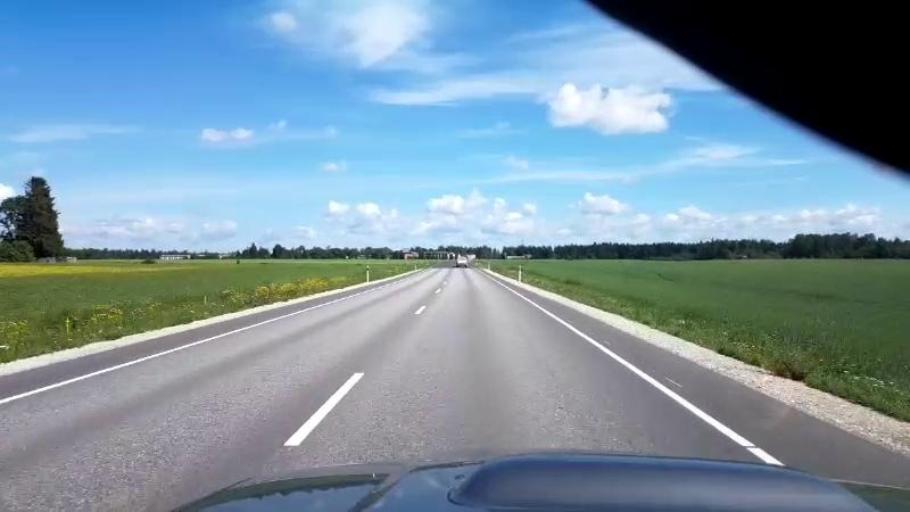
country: EE
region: Jaervamaa
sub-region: Jaerva-Jaani vald
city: Jarva-Jaani
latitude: 59.1192
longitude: 25.7358
